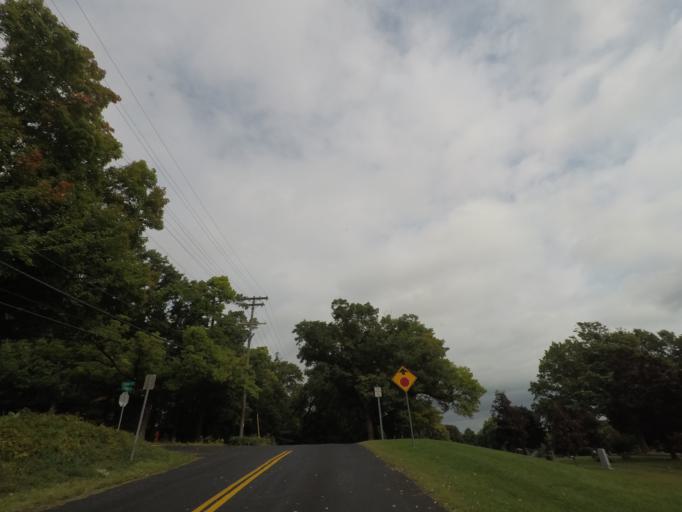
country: US
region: Wisconsin
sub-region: Dane County
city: Shorewood Hills
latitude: 43.0659
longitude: -89.4363
